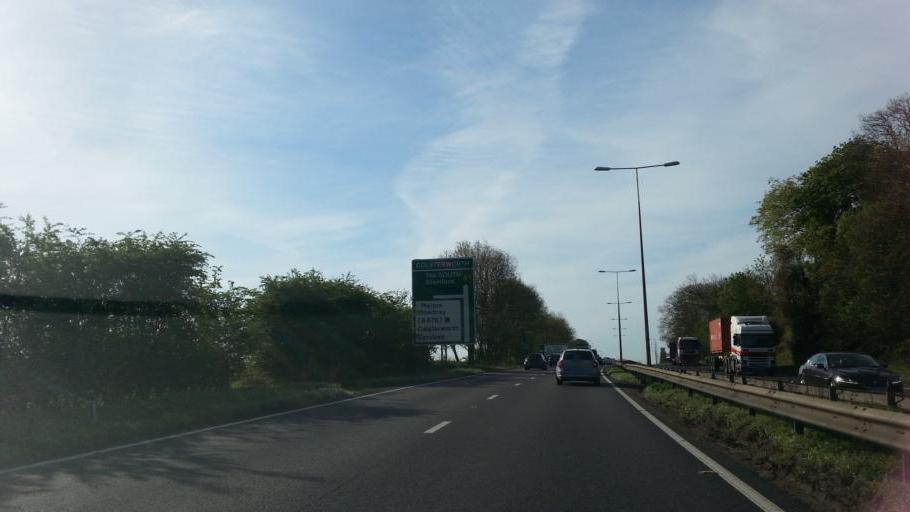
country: GB
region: England
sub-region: District of Rutland
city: Clipsham
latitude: 52.8093
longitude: -0.6148
